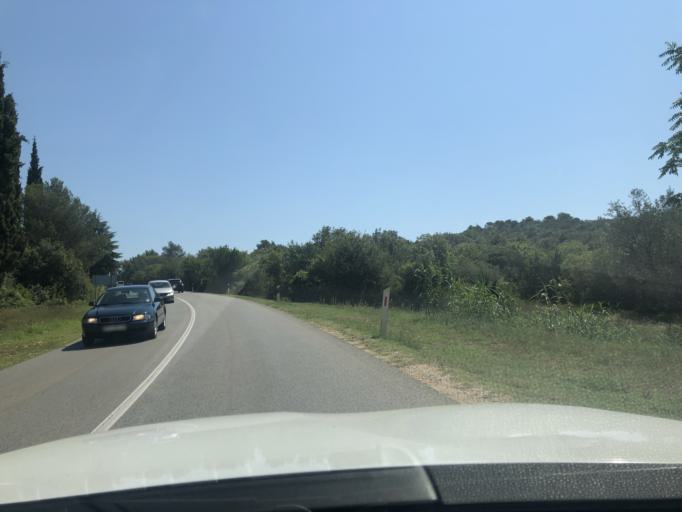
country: HR
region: Istarska
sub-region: Grad Rovinj
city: Rovinj
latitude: 45.0575
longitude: 13.7036
